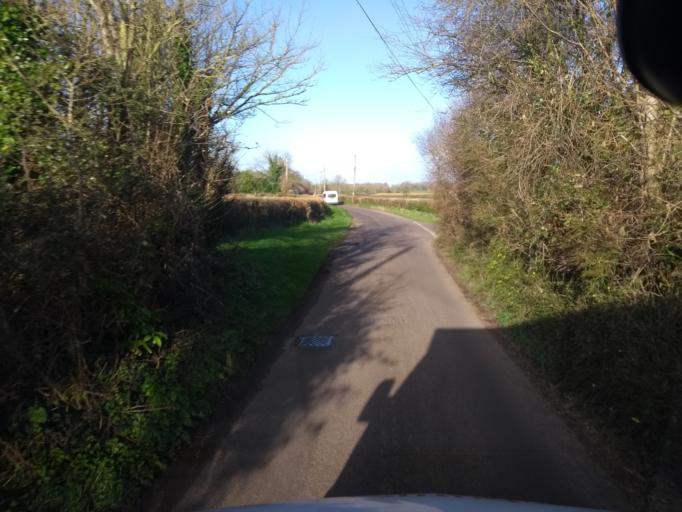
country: GB
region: England
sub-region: Somerset
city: Wedmore
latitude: 51.1354
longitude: -2.8351
